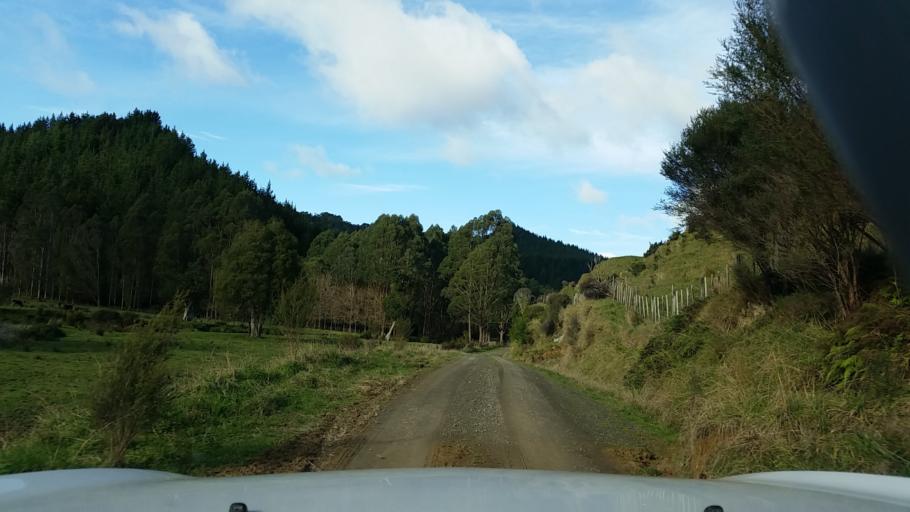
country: NZ
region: Taranaki
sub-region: New Plymouth District
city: Waitara
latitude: -38.9817
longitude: 174.4845
